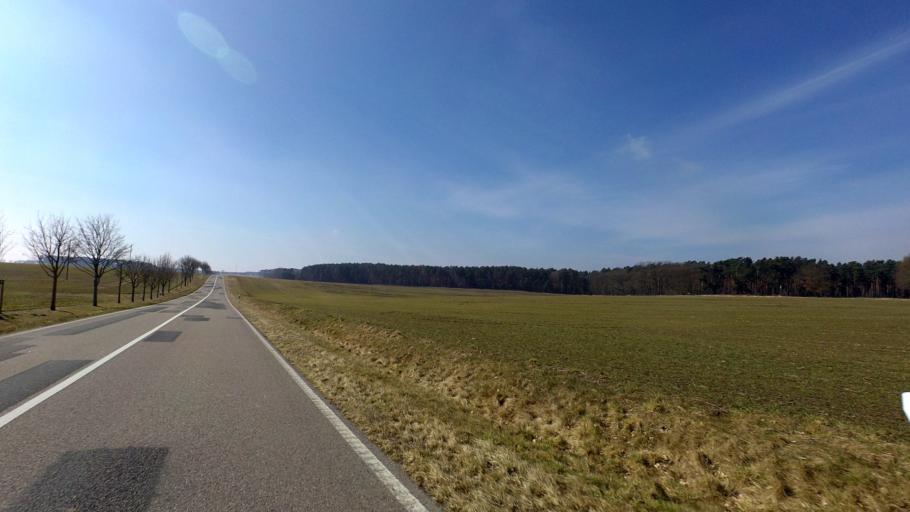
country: DE
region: Brandenburg
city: Wiesenburg
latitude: 52.0700
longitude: 12.5145
